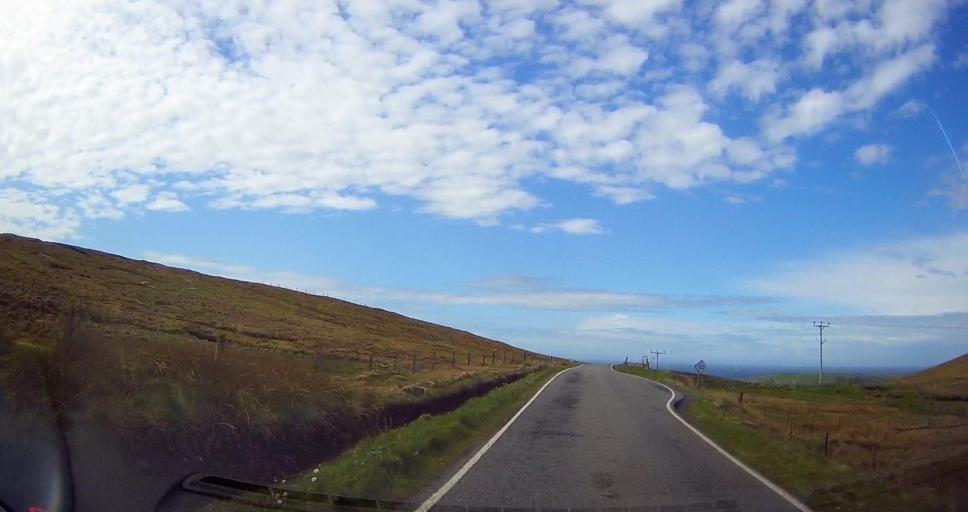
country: GB
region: Scotland
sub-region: Shetland Islands
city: Sandwick
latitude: 59.9798
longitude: -1.2943
